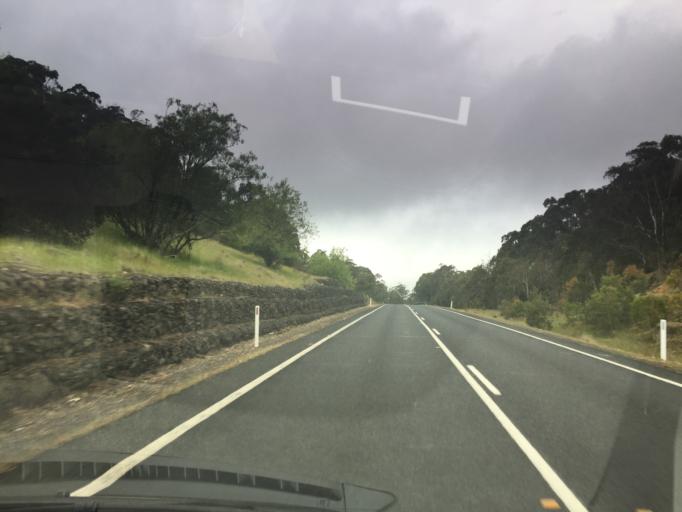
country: AU
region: New South Wales
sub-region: Bombala
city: Bombala
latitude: -36.6000
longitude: 149.3479
